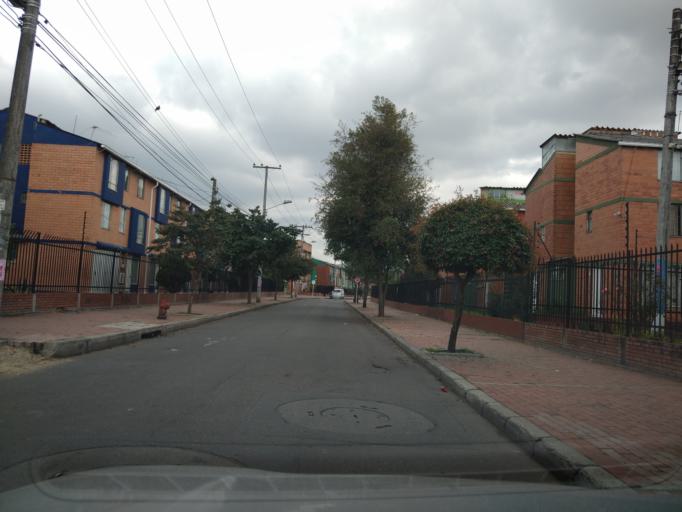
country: CO
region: Cundinamarca
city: Funza
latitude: 4.6702
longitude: -74.1593
